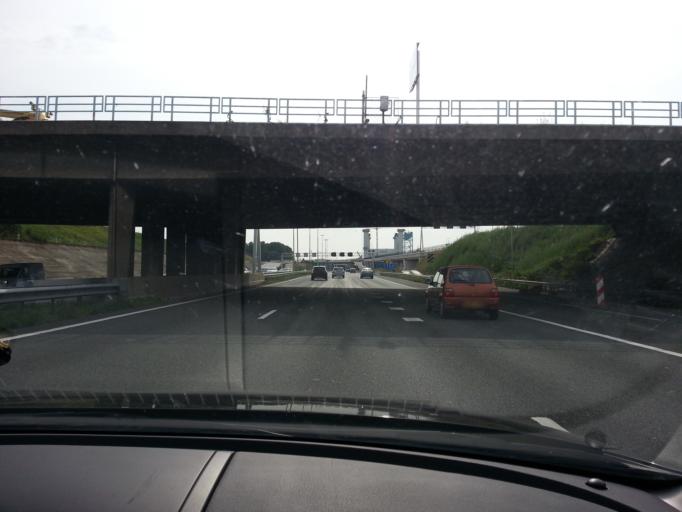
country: NL
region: South Holland
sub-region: Gemeente Spijkenisse
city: Spijkenisse
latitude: 51.8741
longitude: 4.3445
